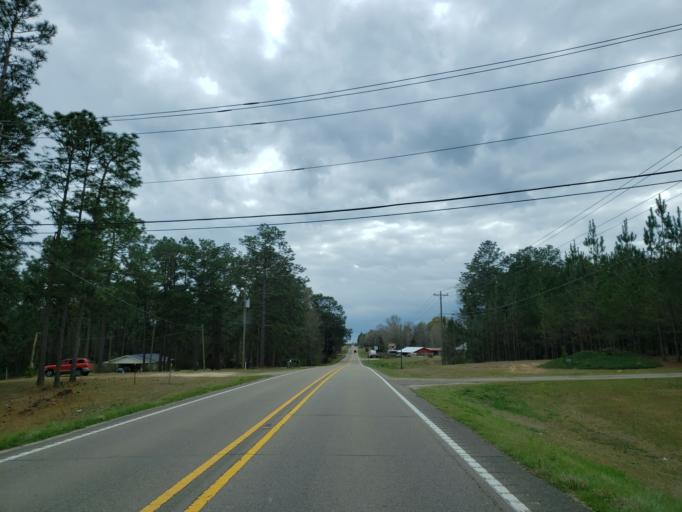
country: US
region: Mississippi
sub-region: Lamar County
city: Purvis
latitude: 31.2127
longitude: -89.3612
